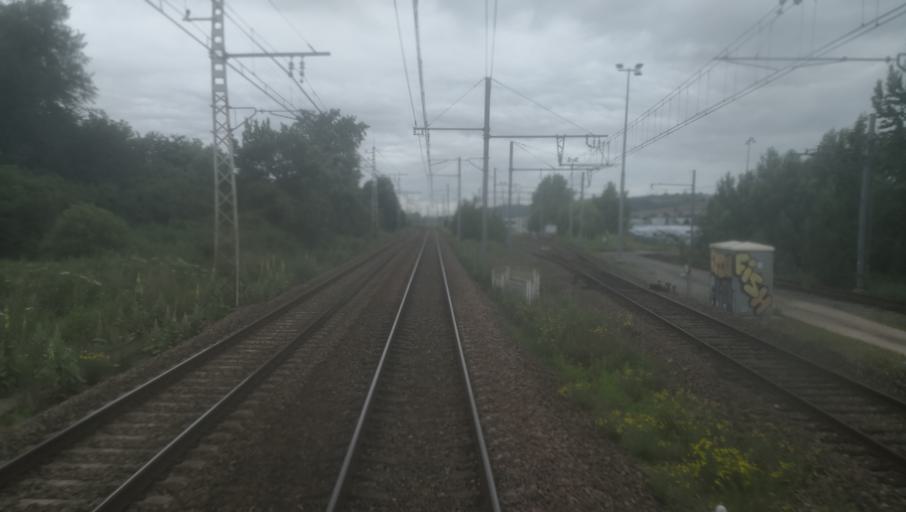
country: FR
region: Midi-Pyrenees
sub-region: Departement de la Haute-Garonne
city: Castelnau-d'Estretefonds
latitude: 43.7729
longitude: 1.3539
